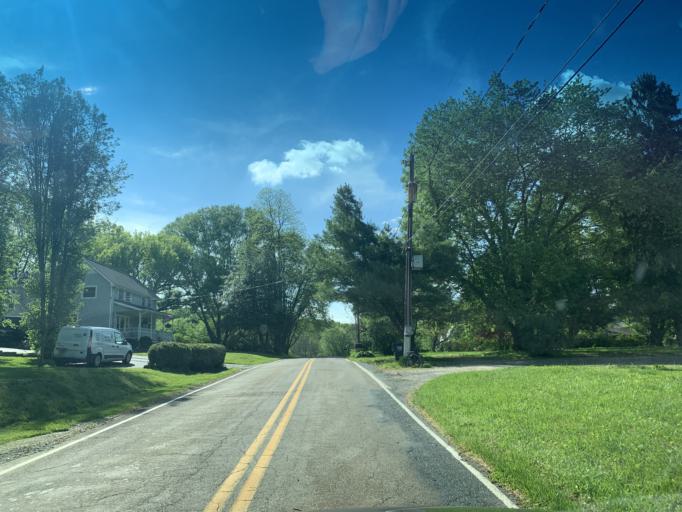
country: US
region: Maryland
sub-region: Cecil County
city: Rising Sun
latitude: 39.6937
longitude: -76.1515
